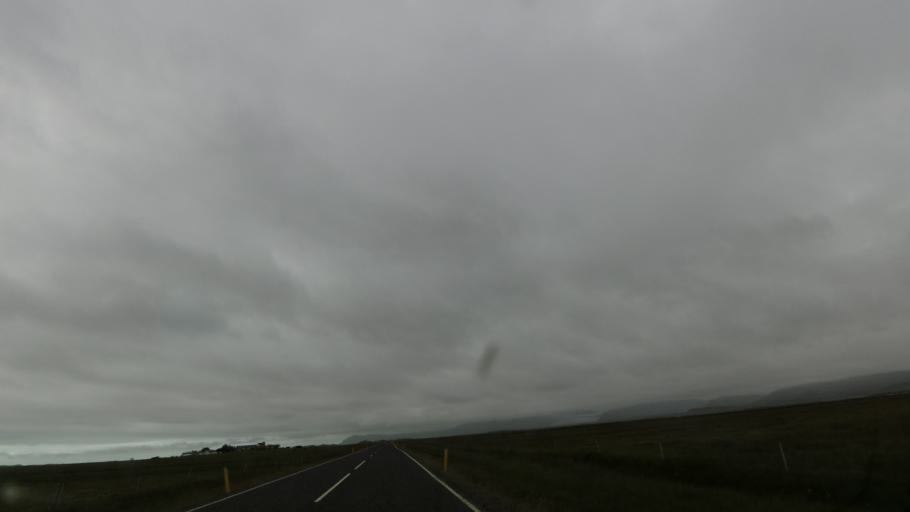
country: IS
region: East
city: Hoefn
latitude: 64.2971
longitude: -15.4281
